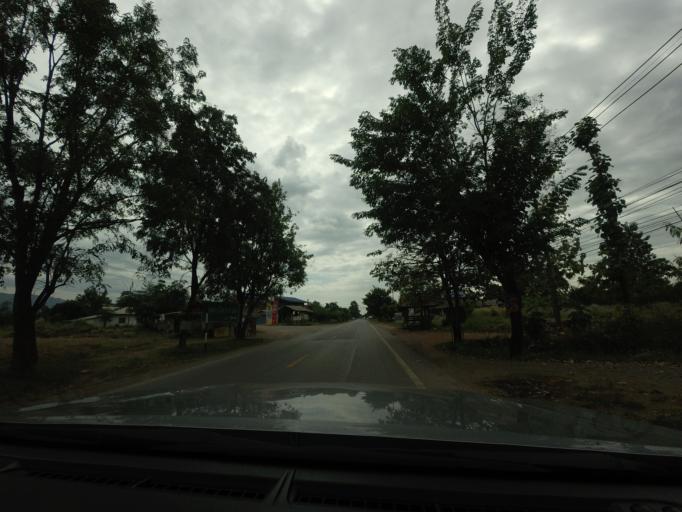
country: TH
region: Phitsanulok
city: Noen Maprang
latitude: 16.6710
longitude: 100.6143
